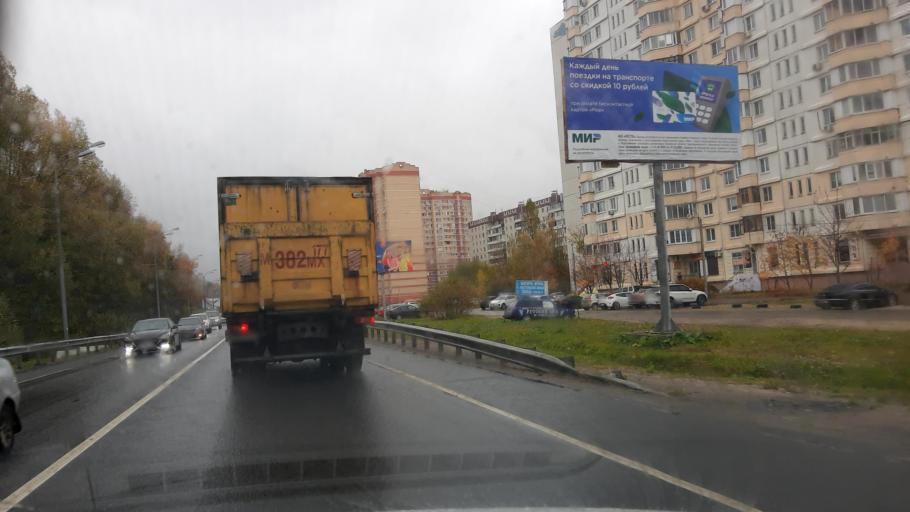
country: RU
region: Moskovskaya
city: Elektrostal'
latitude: 55.8005
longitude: 38.4287
